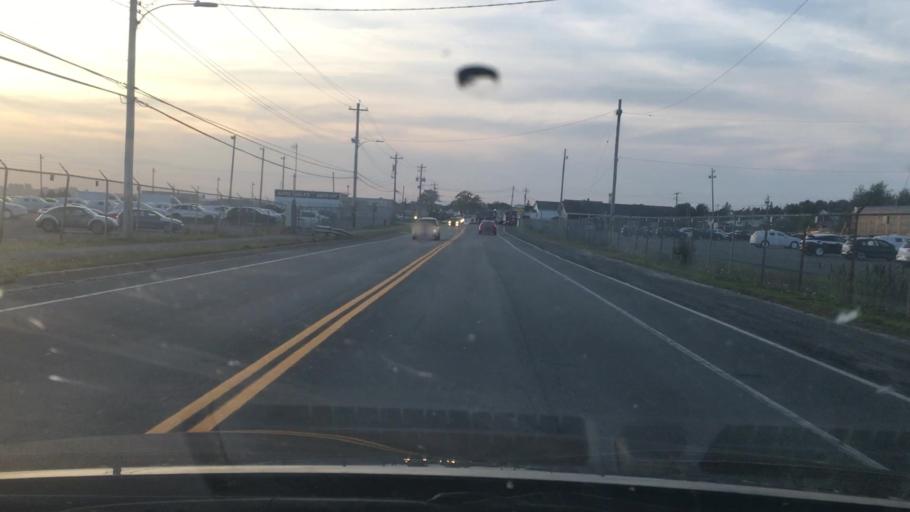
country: CA
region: Nova Scotia
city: Cole Harbour
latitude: 44.6218
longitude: -63.5081
